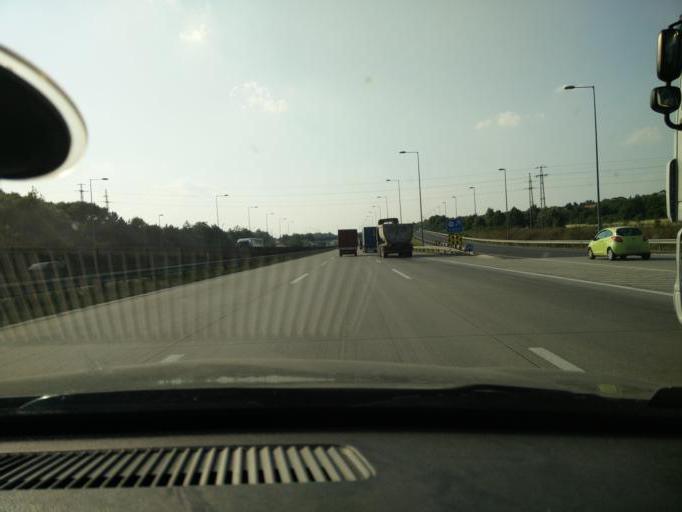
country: HU
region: Pest
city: Diosd
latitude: 47.4089
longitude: 18.9637
